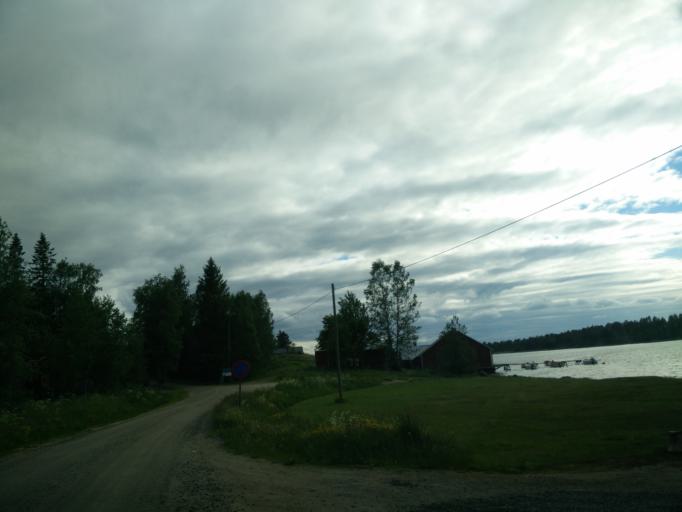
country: SE
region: Vaesternorrland
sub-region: Haernoesands Kommun
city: Haernoesand
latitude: 62.4961
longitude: 17.8132
